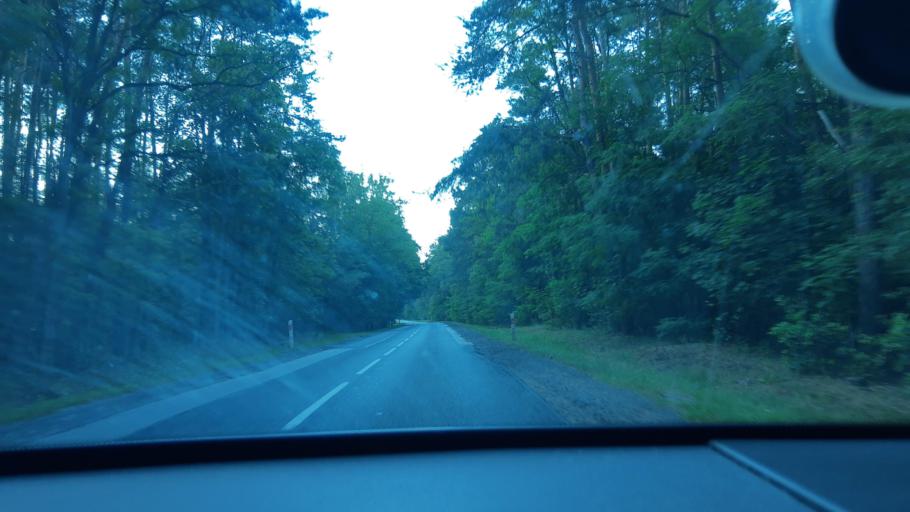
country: PL
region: Lodz Voivodeship
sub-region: Powiat sieradzki
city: Burzenin
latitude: 51.4764
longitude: 18.8290
